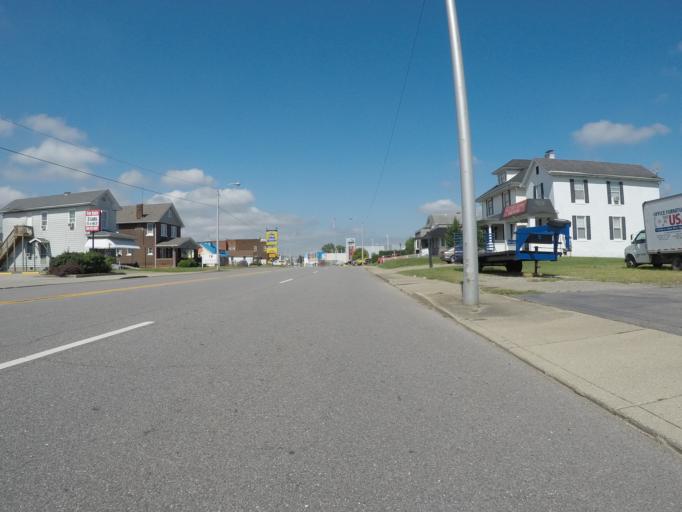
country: US
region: Kentucky
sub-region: Boyd County
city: Ashland
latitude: 38.4712
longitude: -82.6250
